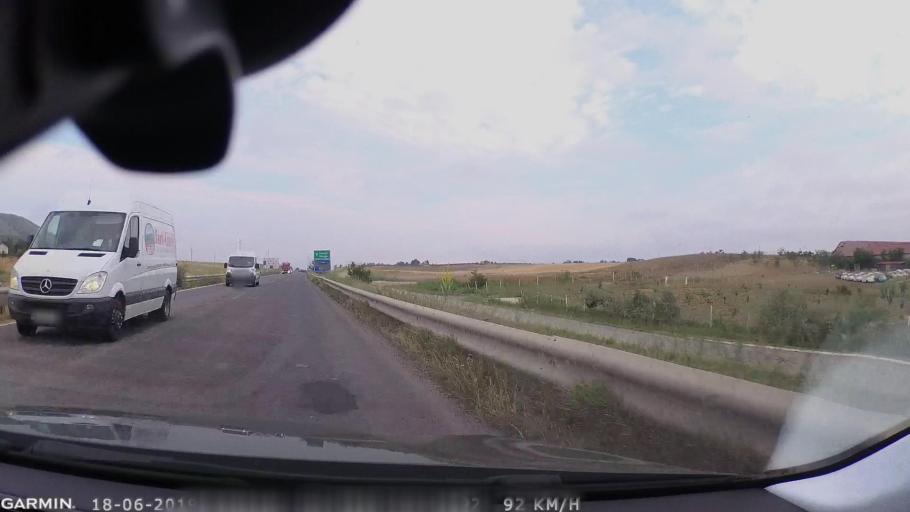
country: MK
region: Stip
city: Shtip
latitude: 41.7767
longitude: 22.1339
